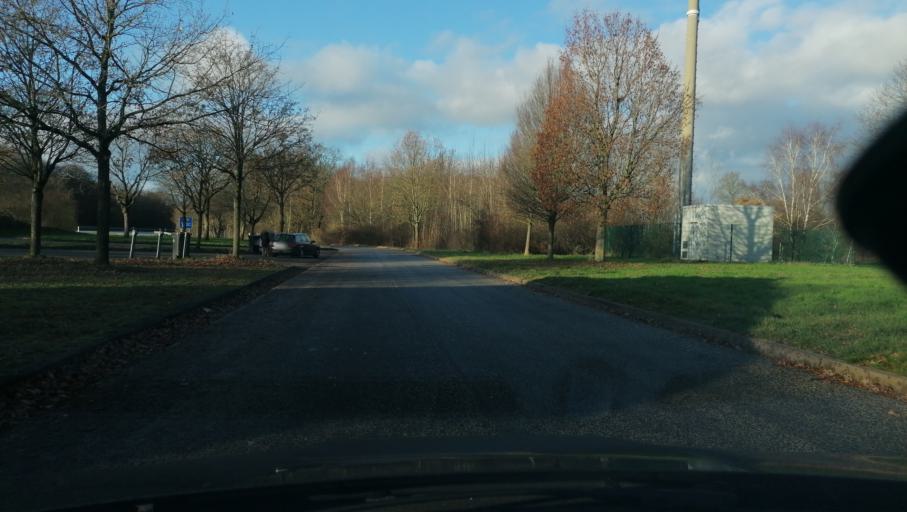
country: DE
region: Schleswig-Holstein
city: Kaisborstel
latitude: 54.0074
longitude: 9.4780
